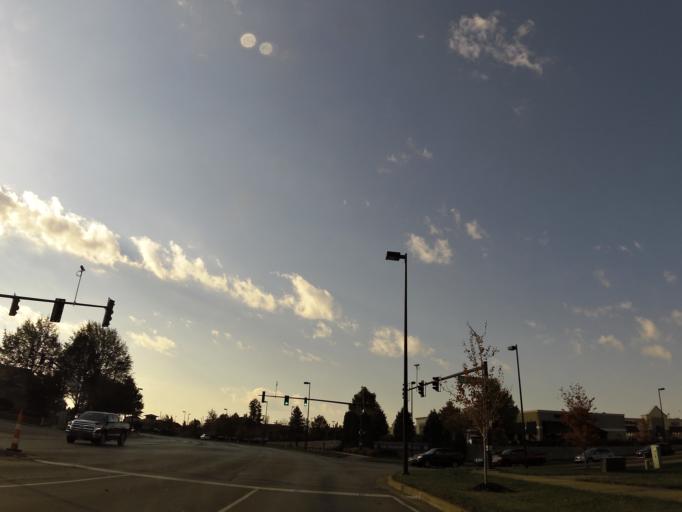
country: US
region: Kentucky
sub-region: Fayette County
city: Lexington-Fayette
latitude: 38.0250
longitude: -84.4232
